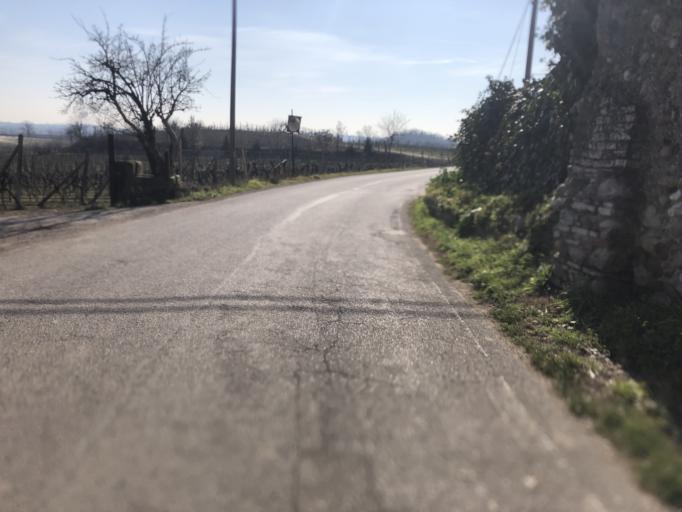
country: IT
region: Veneto
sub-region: Provincia di Verona
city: San Giorgio in Salici
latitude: 45.4055
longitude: 10.7782
